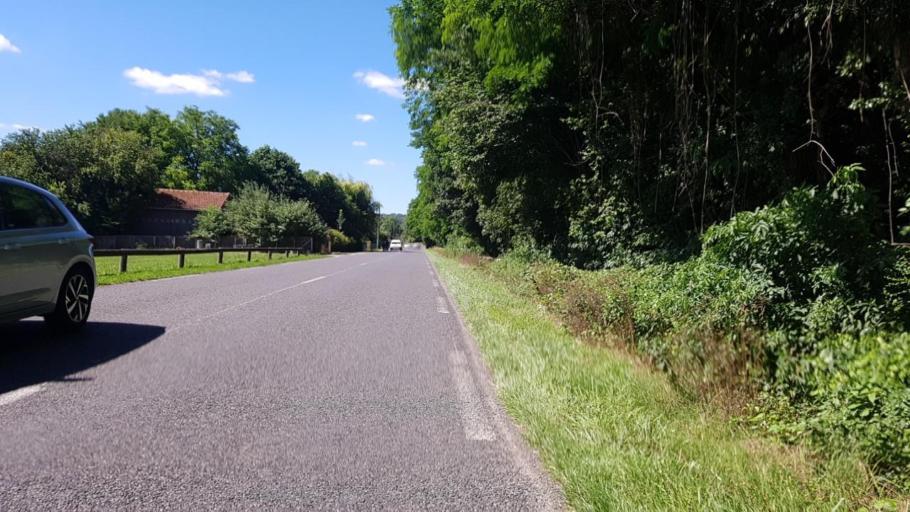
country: FR
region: Ile-de-France
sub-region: Departement de Seine-et-Marne
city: Saacy-sur-Marne
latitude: 48.9698
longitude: 3.2071
